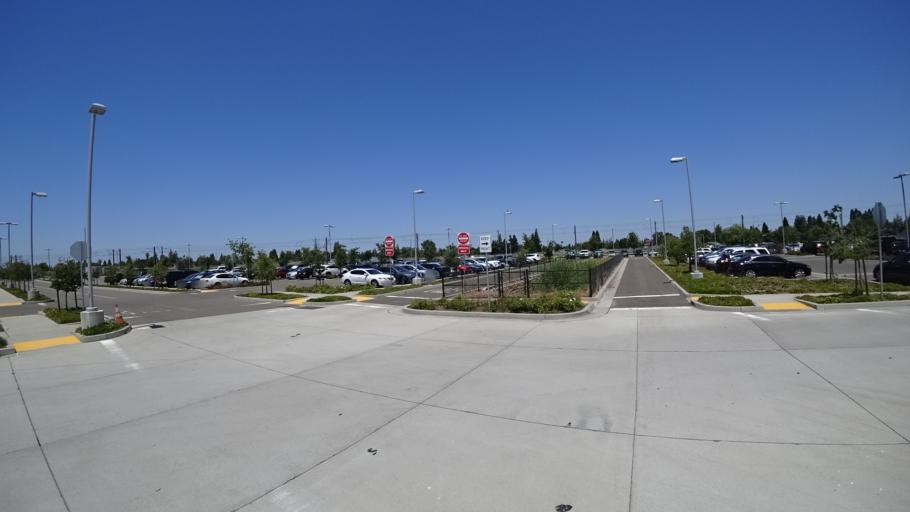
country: US
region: California
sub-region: Sacramento County
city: Parkway
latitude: 38.4626
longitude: -121.4501
